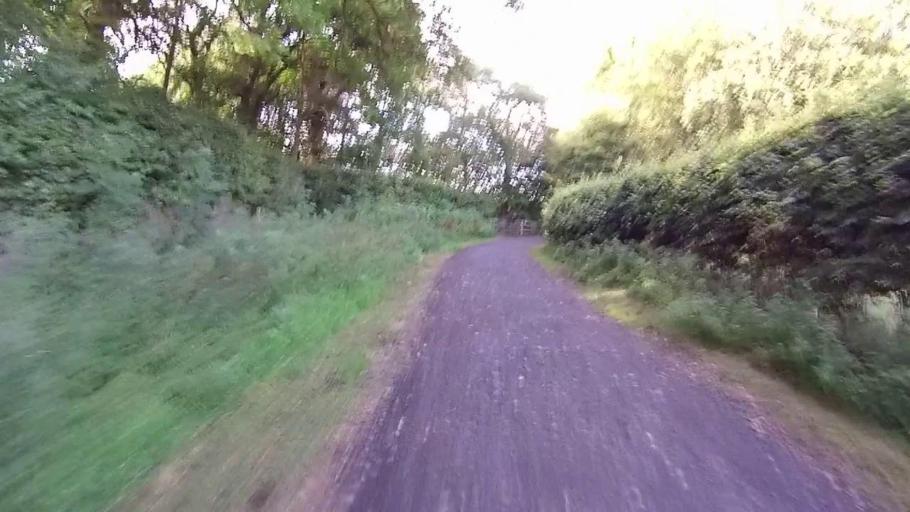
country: GB
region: Scotland
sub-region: Perth and Kinross
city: Kinross
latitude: 56.2042
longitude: -3.4063
